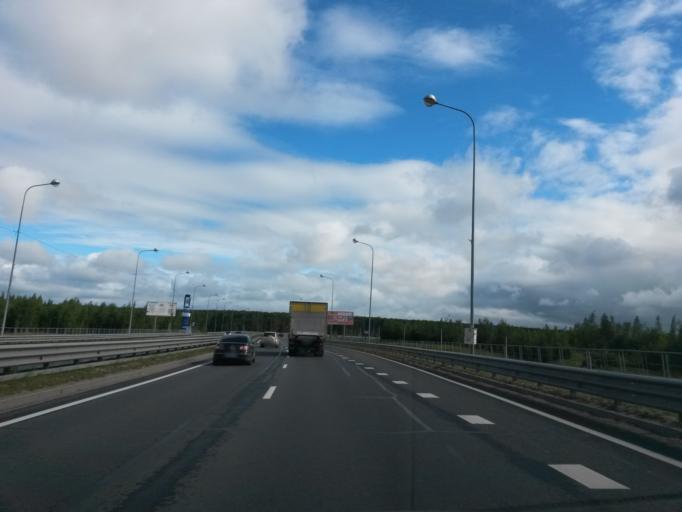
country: RU
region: Jaroslavl
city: Yaroslavl
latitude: 57.6798
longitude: 39.8699
